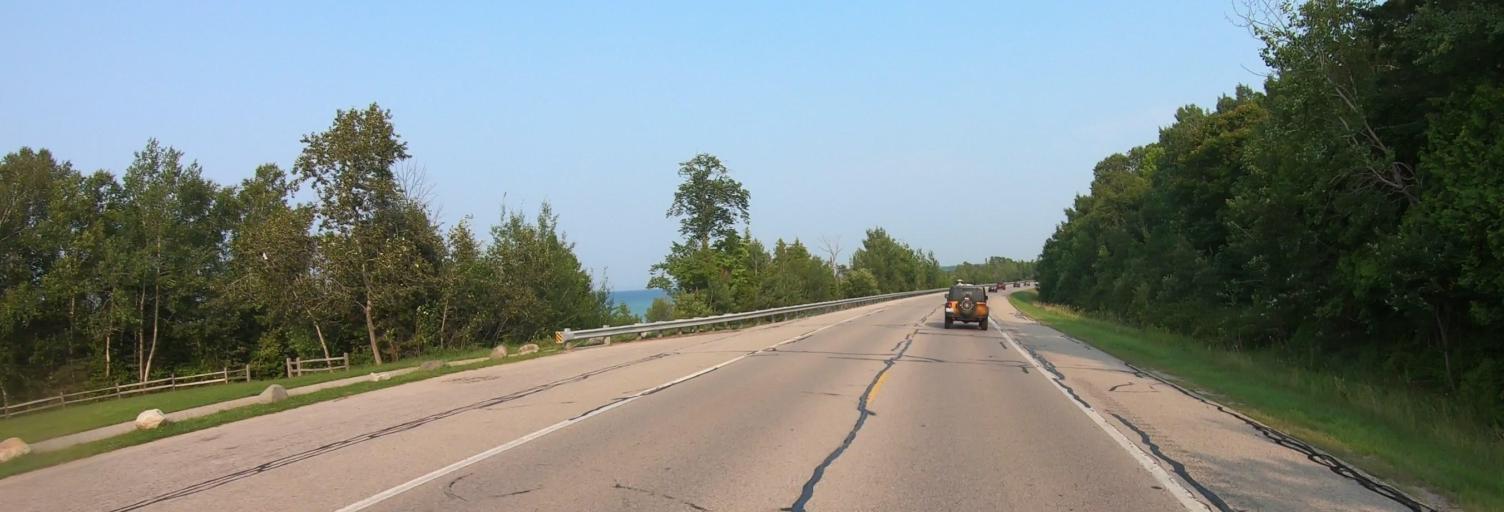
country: US
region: Michigan
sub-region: Charlevoix County
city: Charlevoix
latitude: 45.3680
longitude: -85.1302
